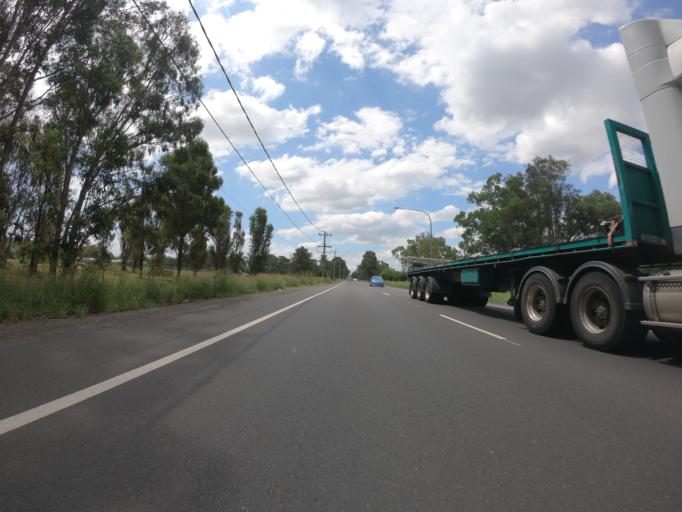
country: AU
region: New South Wales
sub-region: Blacktown
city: Mount Druitt
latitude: -33.7980
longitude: 150.7686
